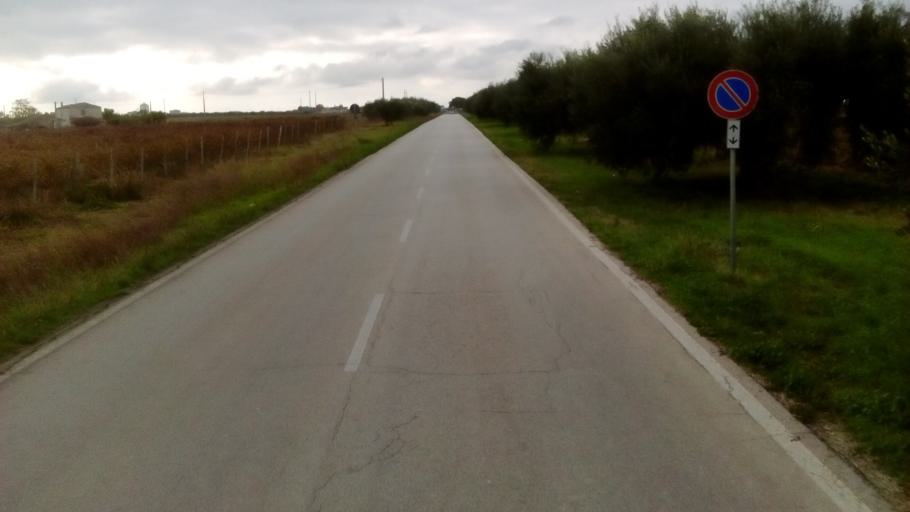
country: IT
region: Abruzzo
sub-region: Provincia di Chieti
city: Vasto
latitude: 42.1553
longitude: 14.7007
